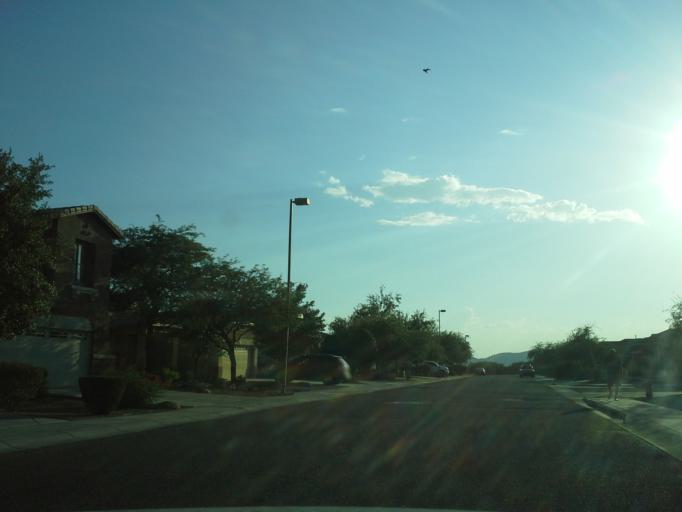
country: US
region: Arizona
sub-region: Maricopa County
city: Anthem
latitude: 33.8645
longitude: -112.1579
